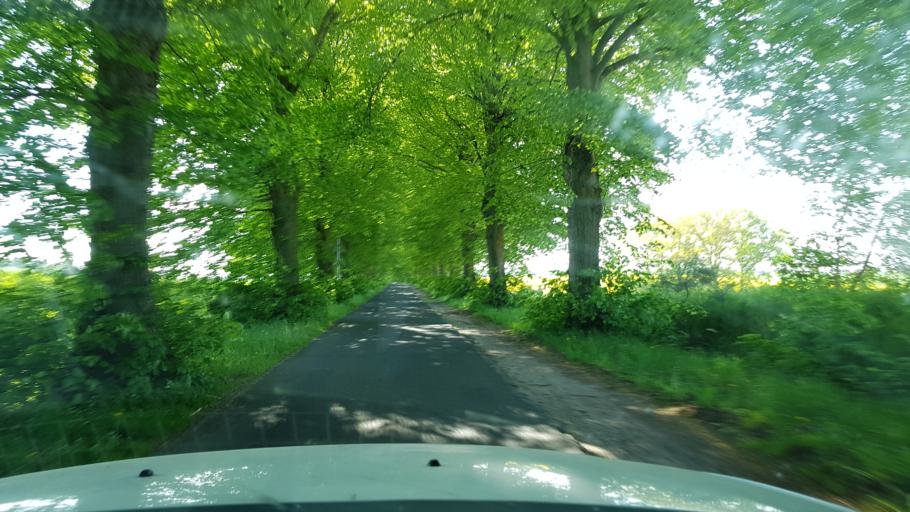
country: PL
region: West Pomeranian Voivodeship
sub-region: Powiat kolobrzeski
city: Goscino
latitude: 54.0102
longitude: 15.6128
